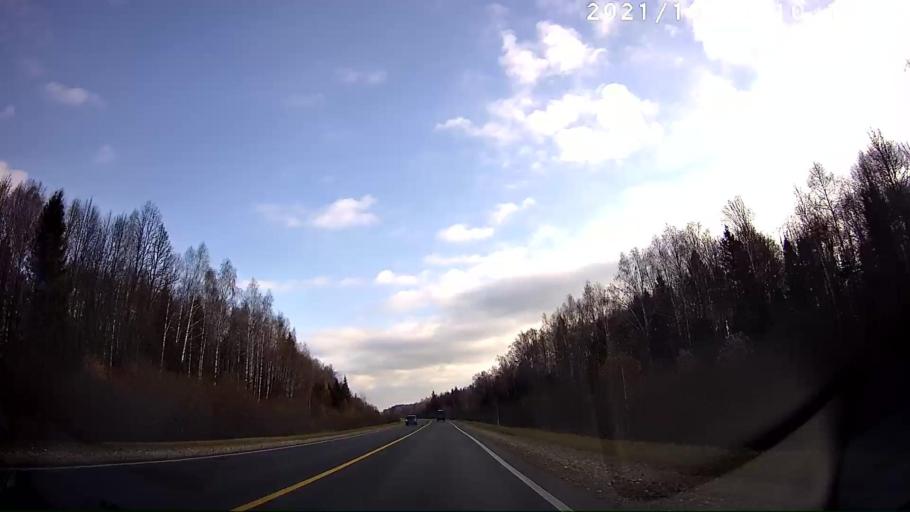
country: RU
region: Mariy-El
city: Sovetskiy
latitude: 56.7386
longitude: 48.4061
